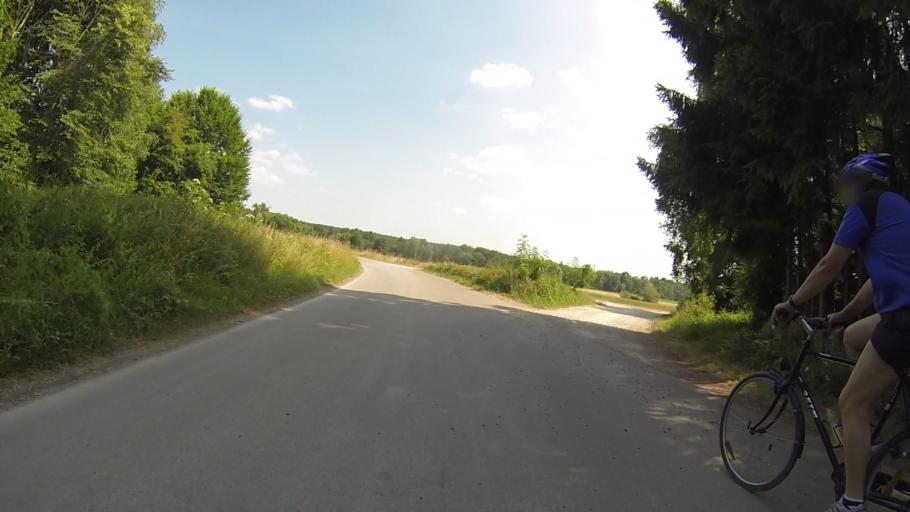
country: DE
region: Bavaria
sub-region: Swabia
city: Guenzburg
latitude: 48.4802
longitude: 10.3068
